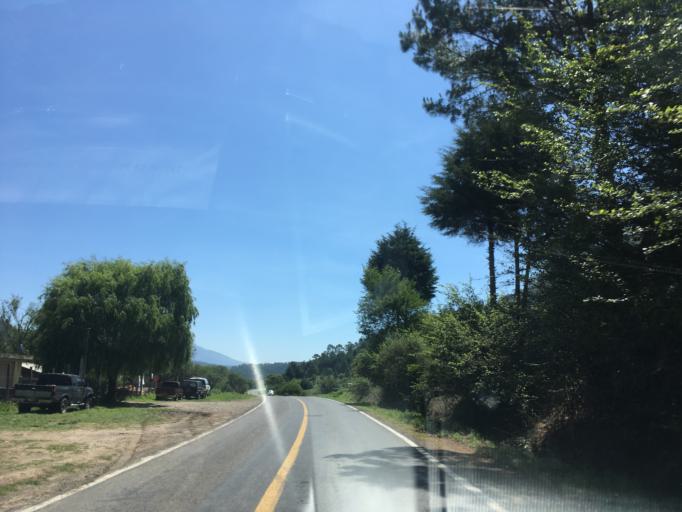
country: MX
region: Michoacan
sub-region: Hidalgo
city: Tierras Coloradas (San Pedro)
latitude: 19.6639
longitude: -100.7535
